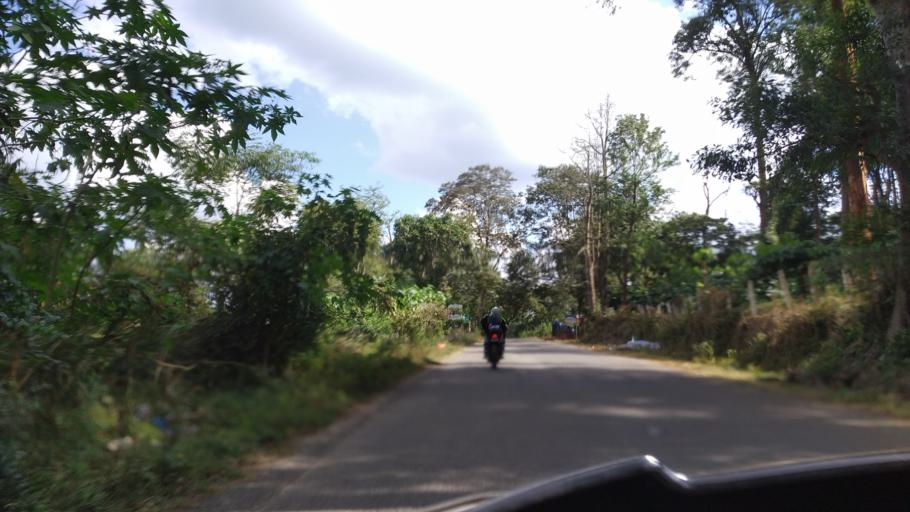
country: IN
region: Karnataka
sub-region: Kodagu
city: Ponnampet
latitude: 11.9605
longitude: 76.0612
